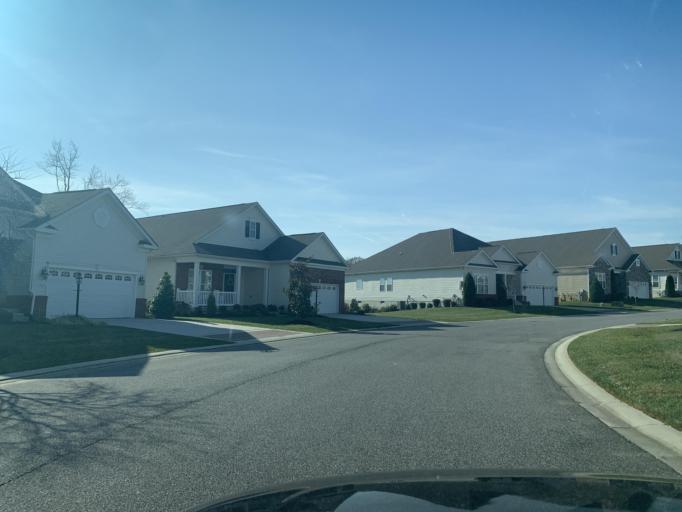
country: US
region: Maryland
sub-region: Harford County
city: Havre de Grace
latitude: 39.5427
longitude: -76.1173
